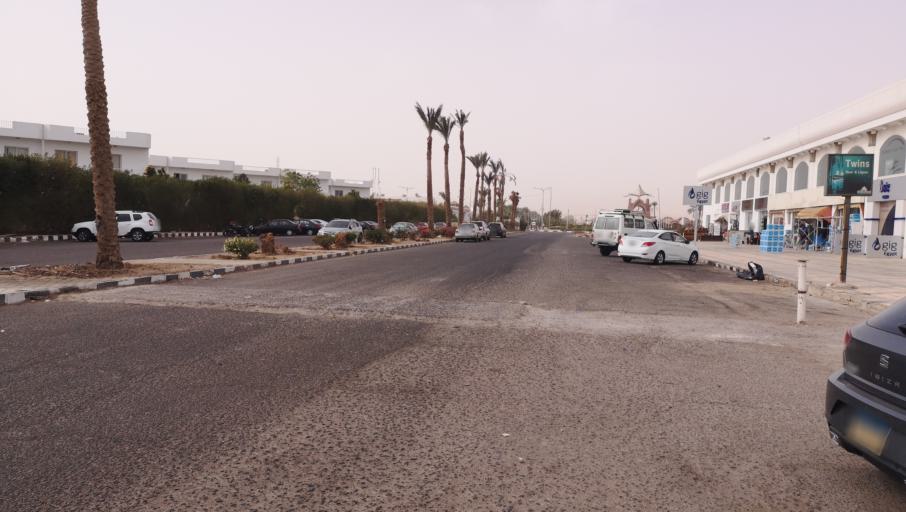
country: EG
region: South Sinai
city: Sharm el-Sheikh
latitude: 27.8655
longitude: 34.3148
